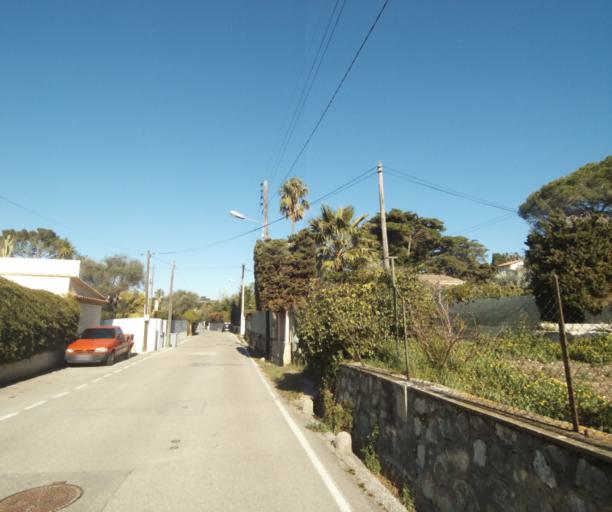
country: FR
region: Provence-Alpes-Cote d'Azur
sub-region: Departement des Alpes-Maritimes
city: Antibes
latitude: 43.5565
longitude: 7.1248
